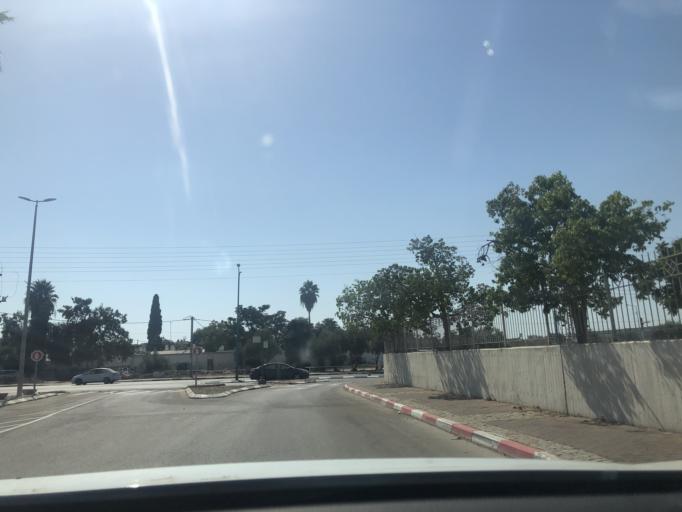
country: IL
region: Central District
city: Lod
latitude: 31.9614
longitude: 34.8998
